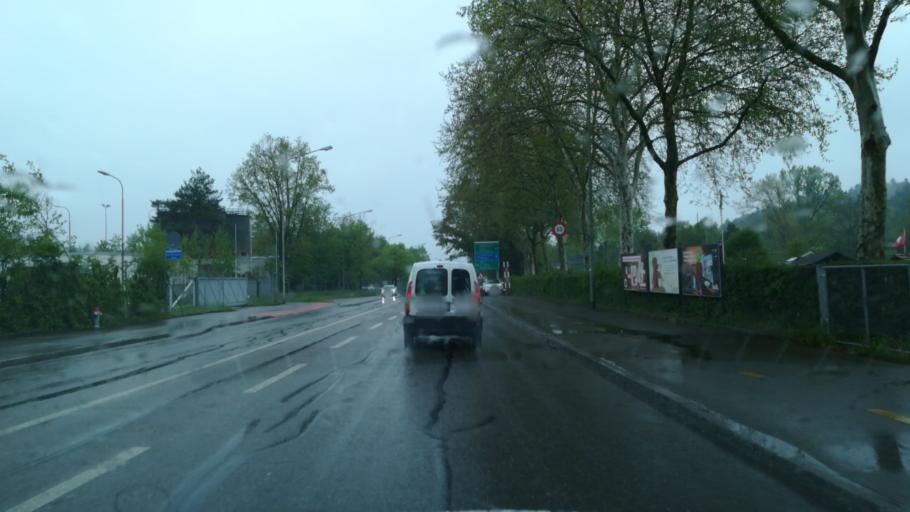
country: CH
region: Zurich
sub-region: Bezirk Winterthur
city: Veltheim
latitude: 47.5205
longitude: 8.7177
